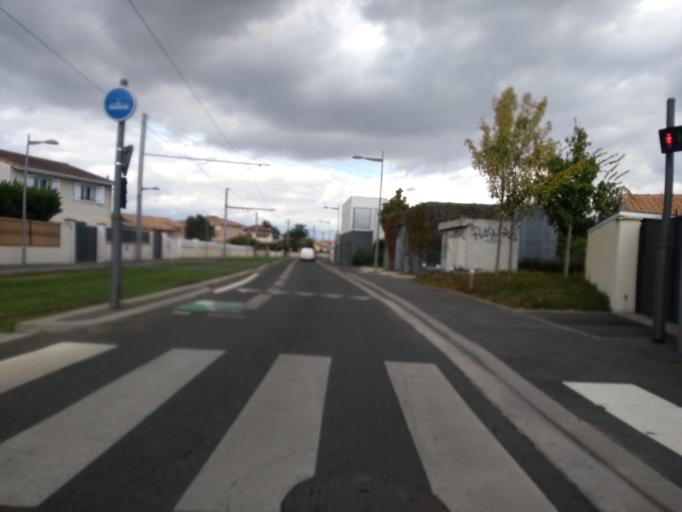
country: FR
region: Aquitaine
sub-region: Departement de la Gironde
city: Begles
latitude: 44.8002
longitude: -0.5515
